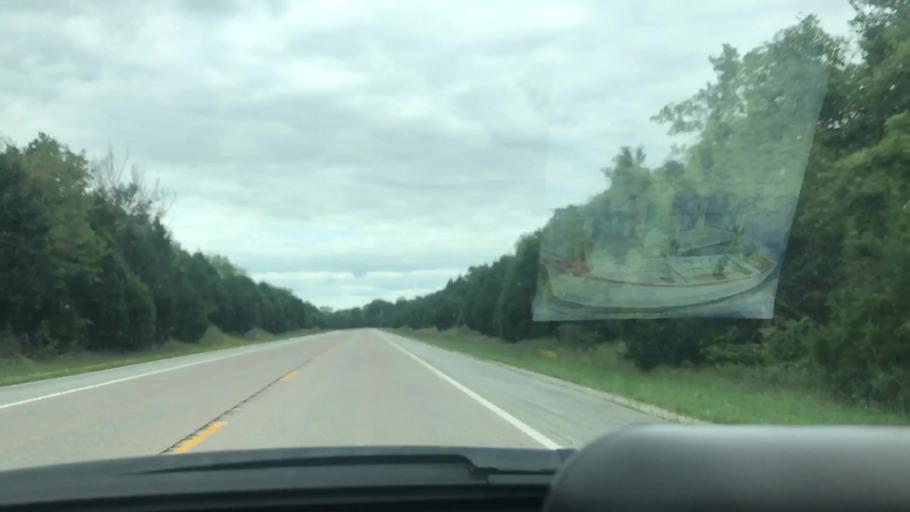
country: US
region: Missouri
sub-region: Benton County
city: Warsaw
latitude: 38.1995
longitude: -93.3256
